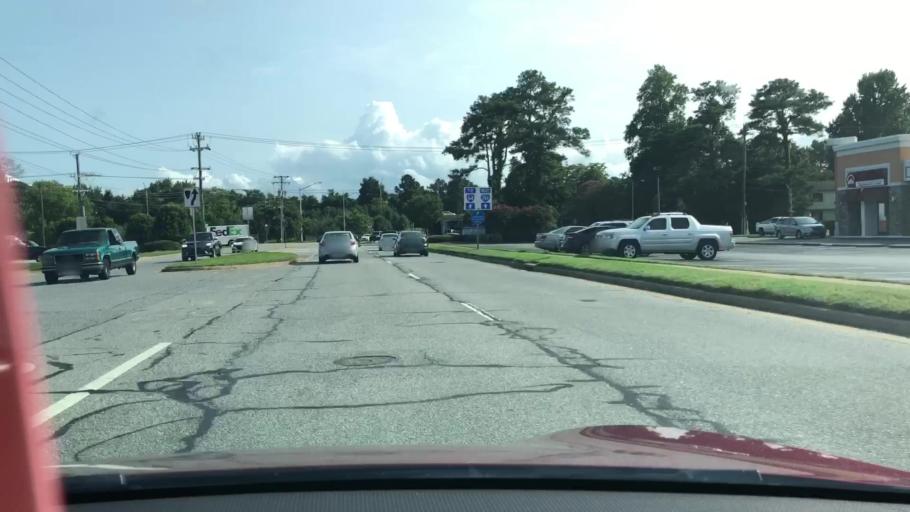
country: US
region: Virginia
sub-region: City of Virginia Beach
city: Virginia Beach
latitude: 36.8488
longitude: -75.9943
